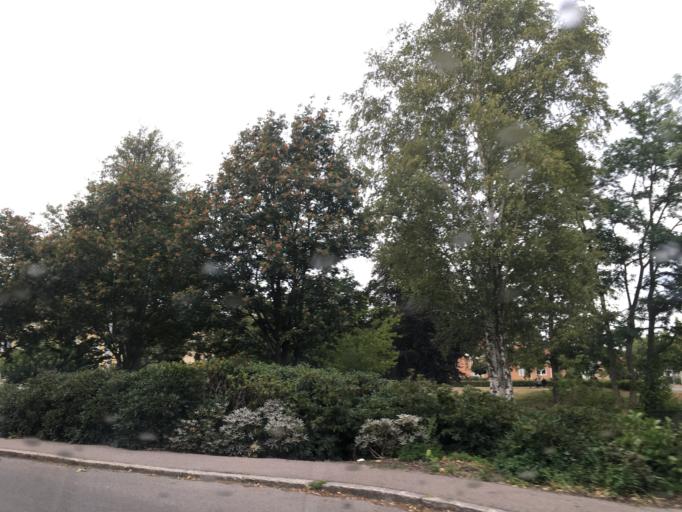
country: SE
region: Kalmar
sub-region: Nybro Kommun
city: Nybro
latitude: 56.7449
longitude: 15.9061
